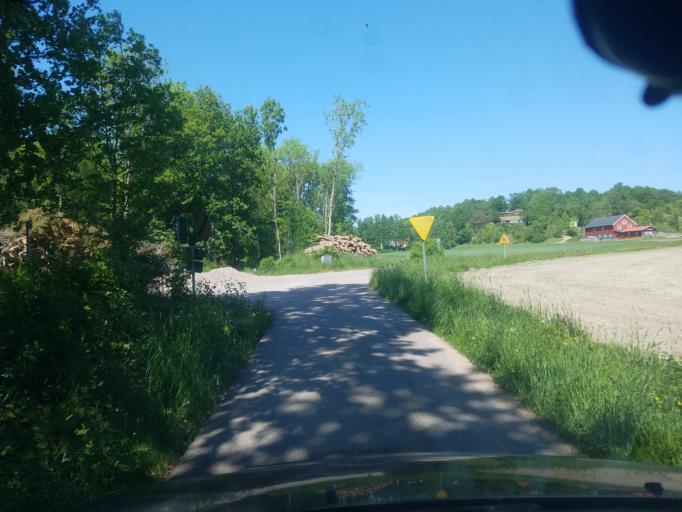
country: SE
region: Vaestra Goetaland
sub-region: Orust
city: Henan
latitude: 58.2658
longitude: 11.5713
